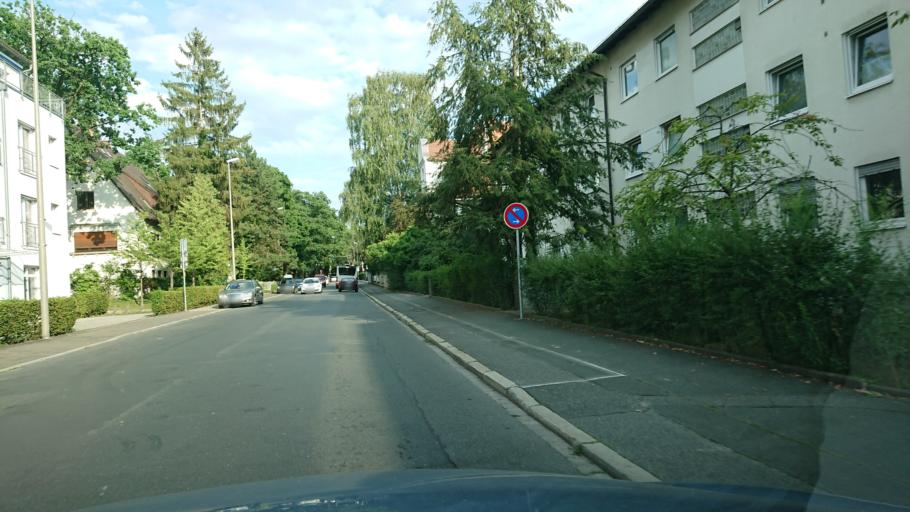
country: DE
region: Bavaria
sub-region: Regierungsbezirk Mittelfranken
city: Erlangen
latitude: 49.6059
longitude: 11.0126
